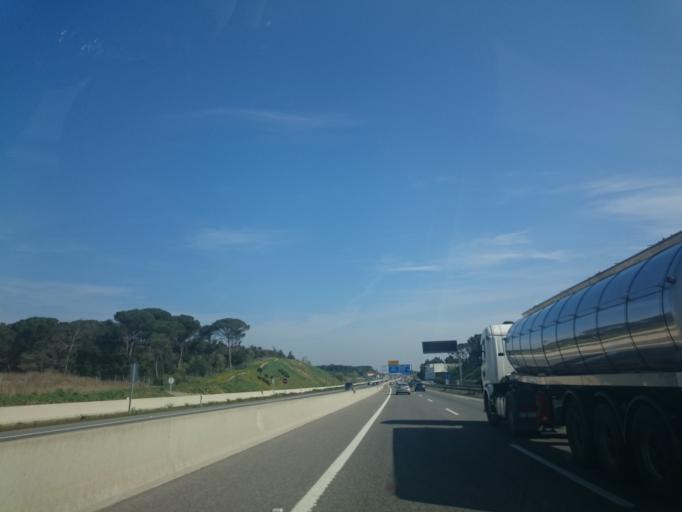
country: ES
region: Catalonia
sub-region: Provincia de Girona
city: Riudellots de la Selva
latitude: 41.9096
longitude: 2.7899
